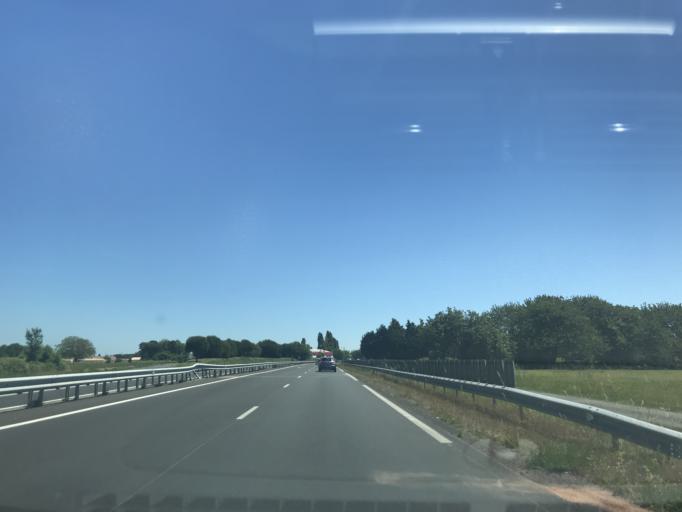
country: FR
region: Poitou-Charentes
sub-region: Departement de la Charente-Maritime
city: Vaux-sur-Mer
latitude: 45.6526
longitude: -1.0514
